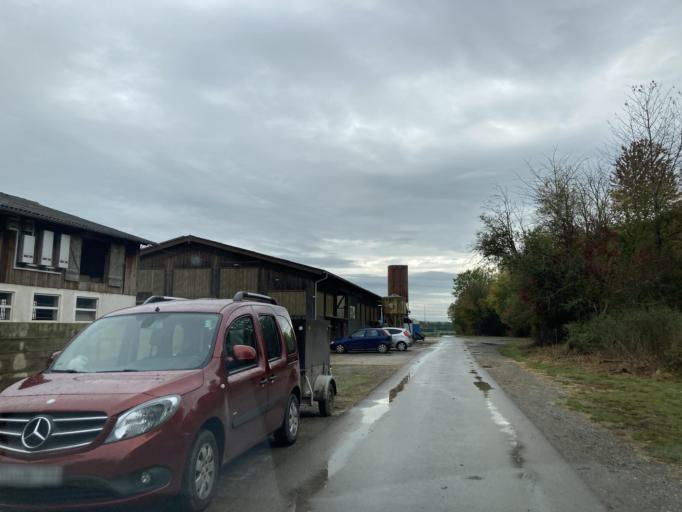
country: DE
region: Baden-Wuerttemberg
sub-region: Regierungsbezirk Stuttgart
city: Bondorf
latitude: 48.5378
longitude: 8.8568
